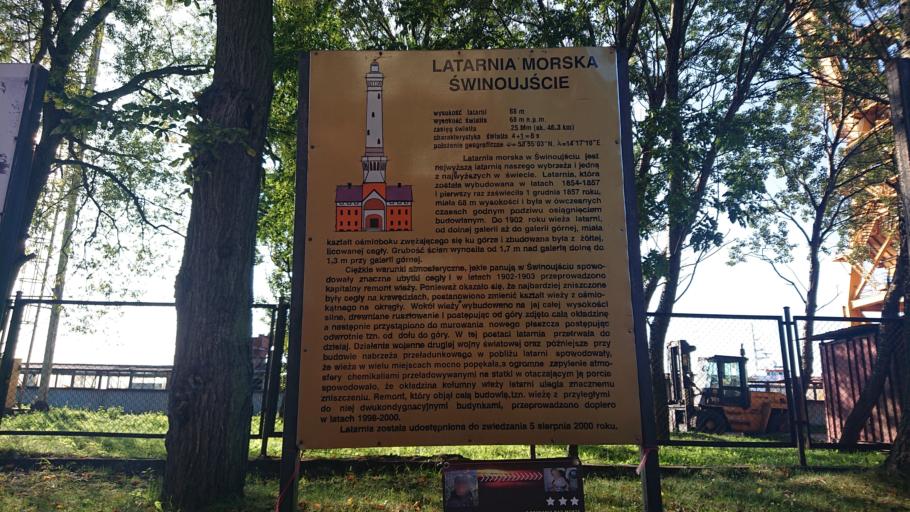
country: PL
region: West Pomeranian Voivodeship
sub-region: Swinoujscie
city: Swinoujscie
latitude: 53.9162
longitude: 14.2840
